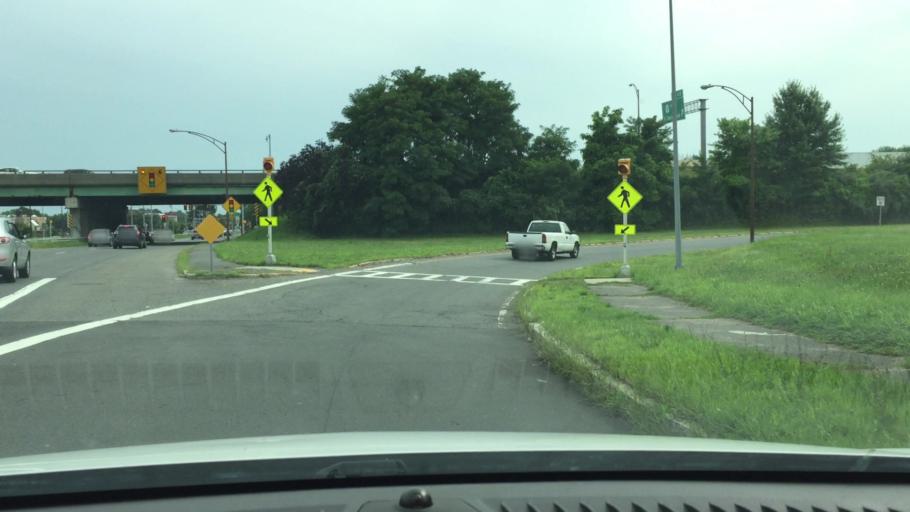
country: US
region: Massachusetts
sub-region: Hampden County
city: Chicopee
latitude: 42.1372
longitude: -72.6259
